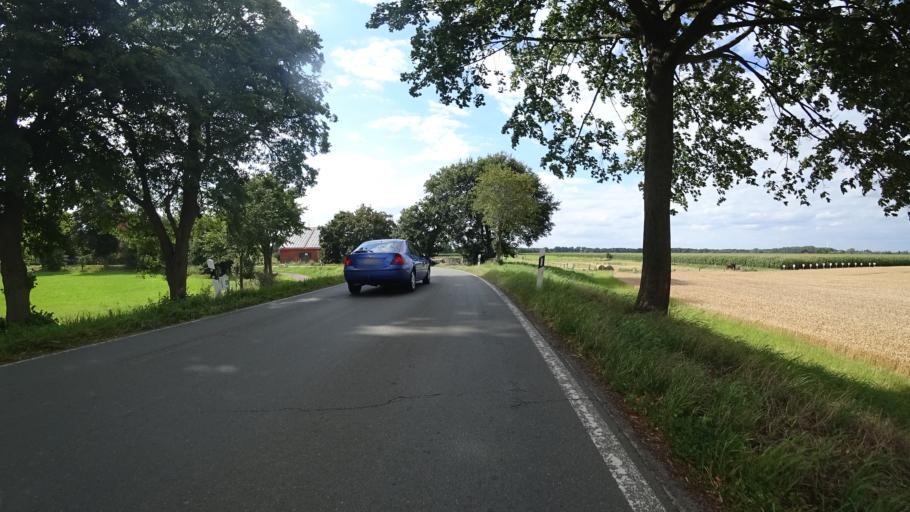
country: DE
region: Lower Saxony
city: Stolzenau
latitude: 52.4837
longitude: 9.0754
